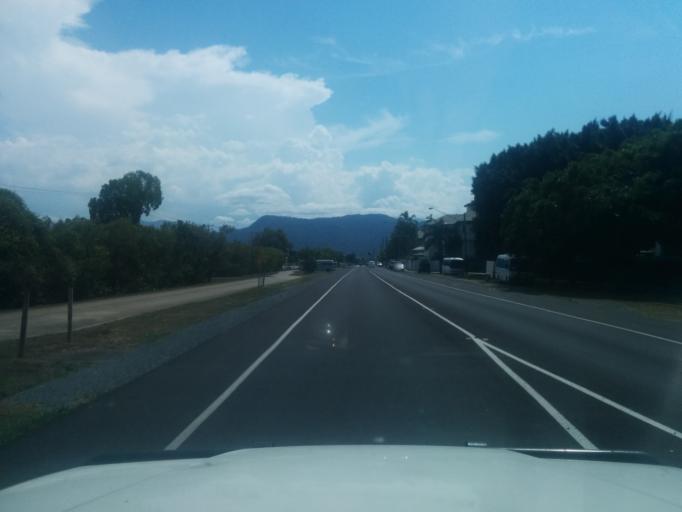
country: AU
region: Queensland
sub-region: Cairns
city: Cairns
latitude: -16.9318
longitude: 145.7670
